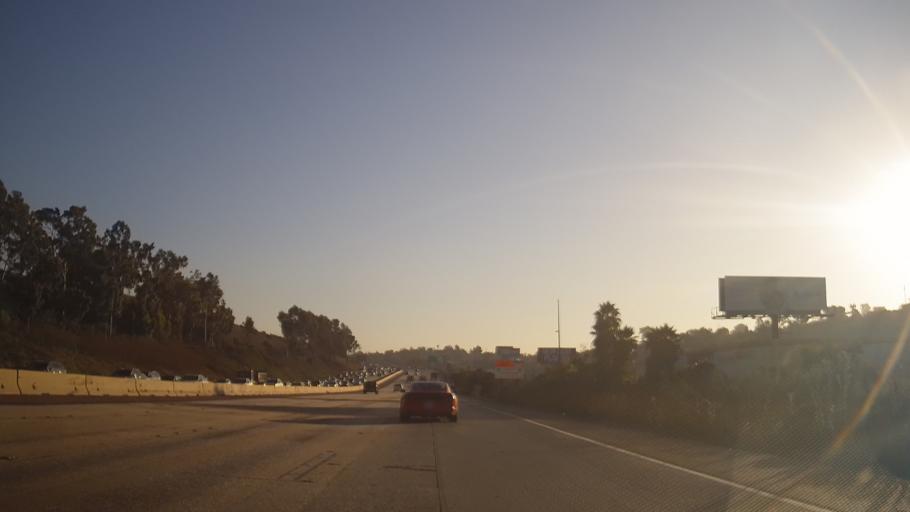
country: US
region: California
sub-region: San Diego County
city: Lemon Grove
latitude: 32.7276
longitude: -117.0700
